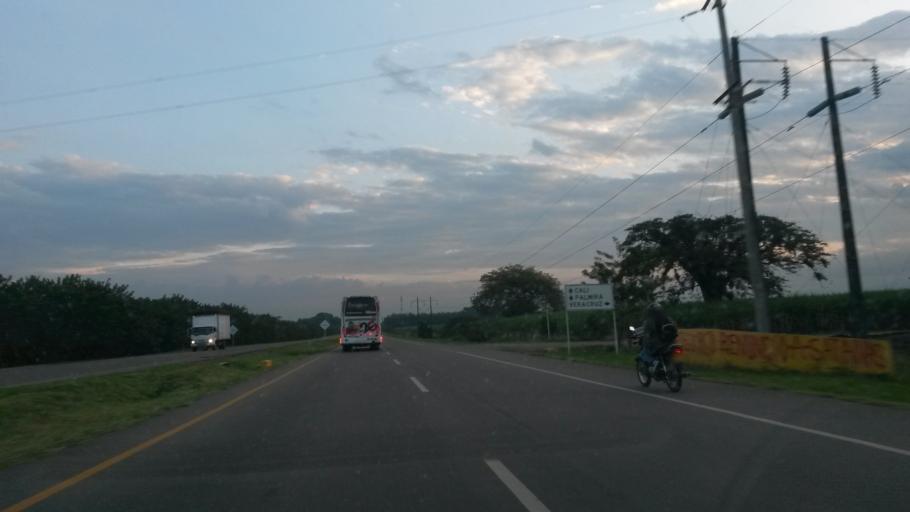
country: CO
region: Cauca
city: Caloto
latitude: 3.1050
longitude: -76.4682
